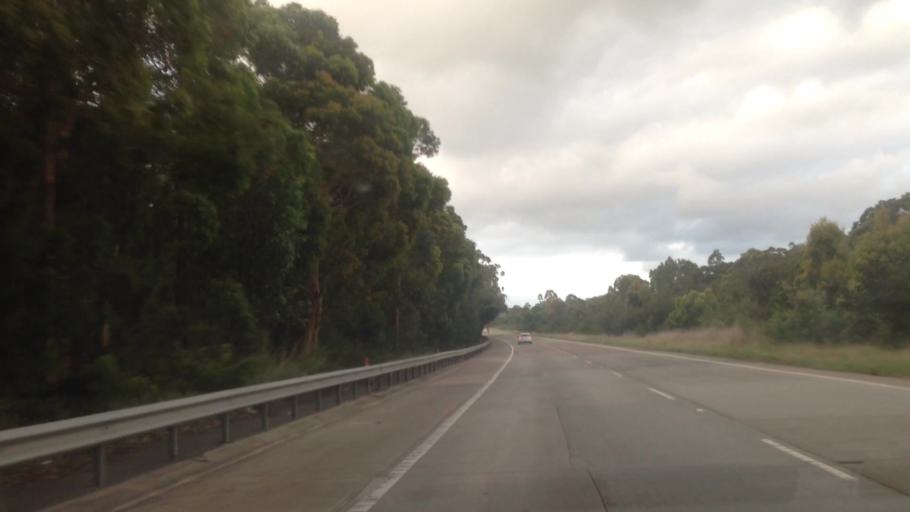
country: AU
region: New South Wales
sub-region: Wyong Shire
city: Charmhaven
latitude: -33.1876
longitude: 151.4675
